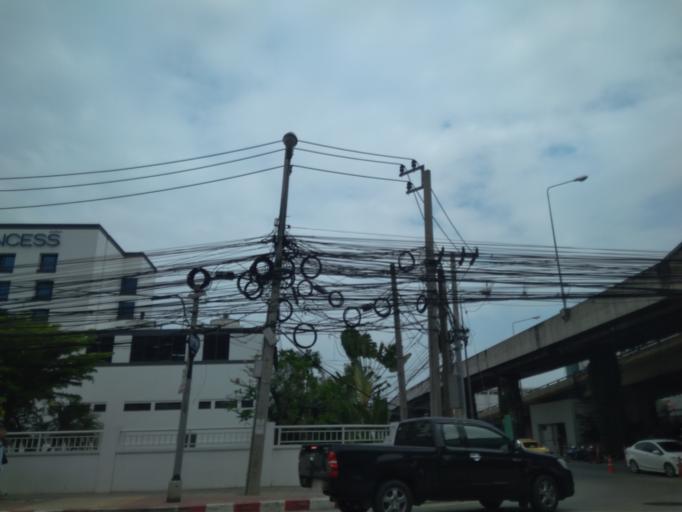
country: TH
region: Bangkok
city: Bang Na
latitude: 13.6968
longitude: 100.6475
